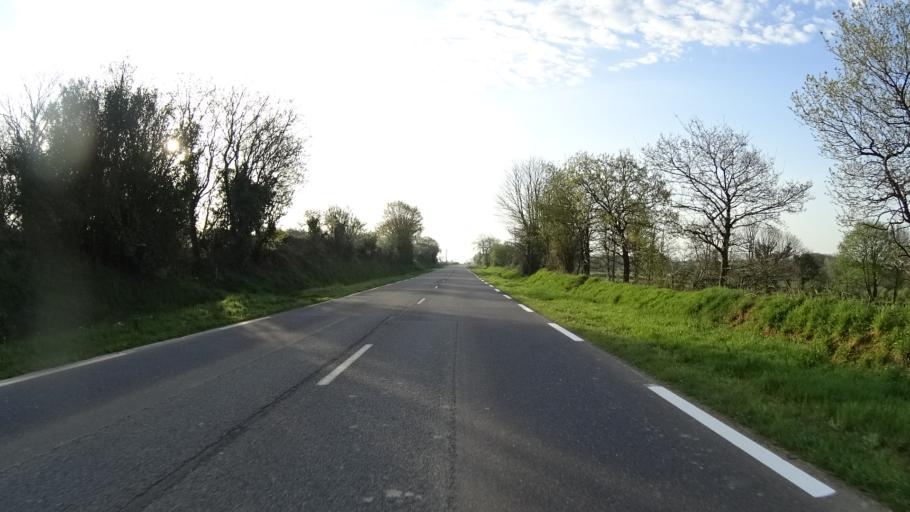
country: FR
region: Brittany
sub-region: Departement du Finistere
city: La Roche-Maurice
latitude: 48.4349
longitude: -4.1576
